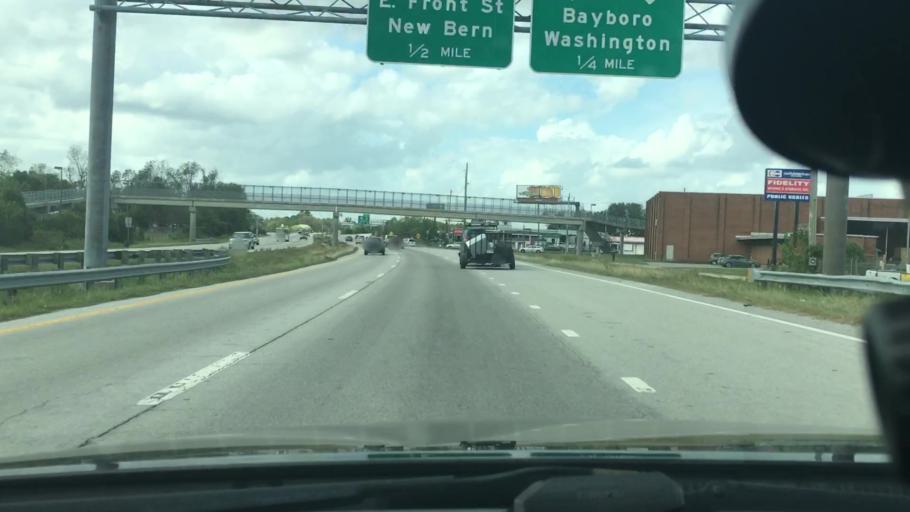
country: US
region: North Carolina
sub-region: Craven County
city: James City
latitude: 35.0862
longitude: -77.0328
